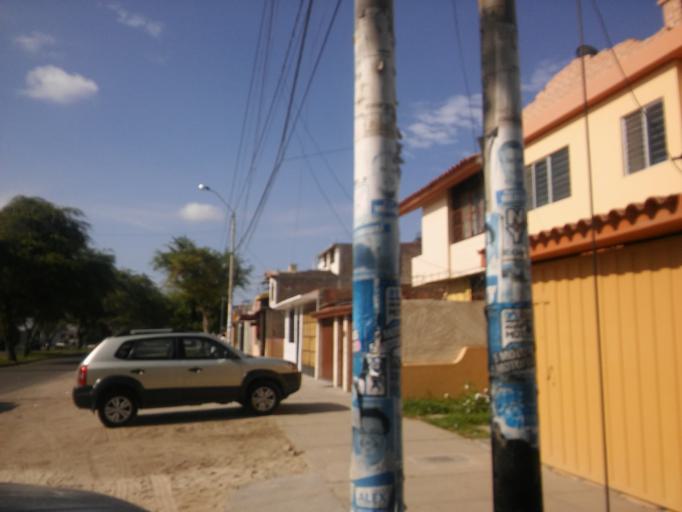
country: PE
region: Piura
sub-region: Provincia de Piura
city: Piura
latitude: -5.1884
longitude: -80.6421
